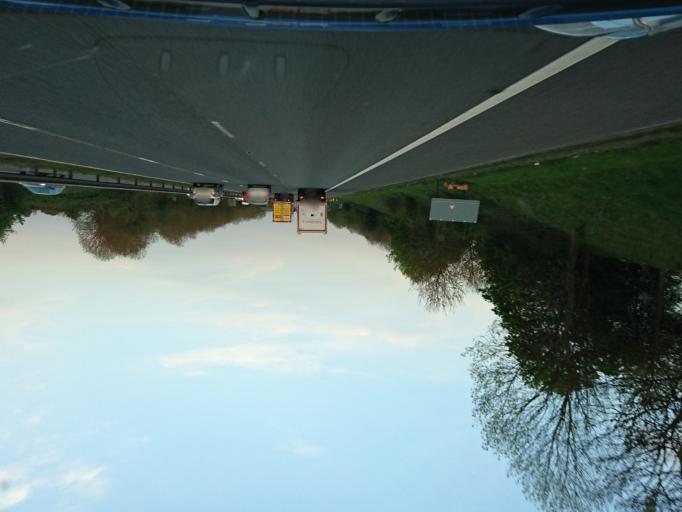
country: GB
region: England
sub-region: Warwickshire
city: Rugby
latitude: 52.4069
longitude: -1.2284
